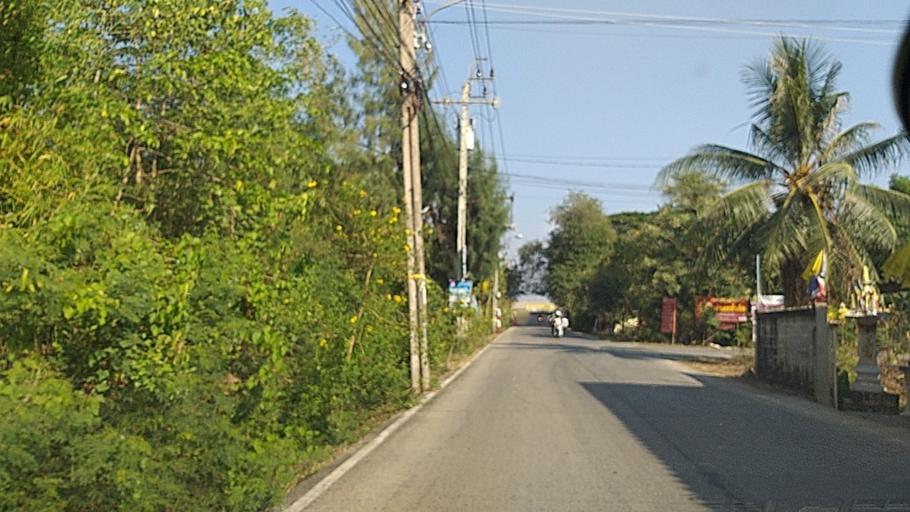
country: TH
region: Nonthaburi
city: Sai Noi
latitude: 13.9348
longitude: 100.3430
